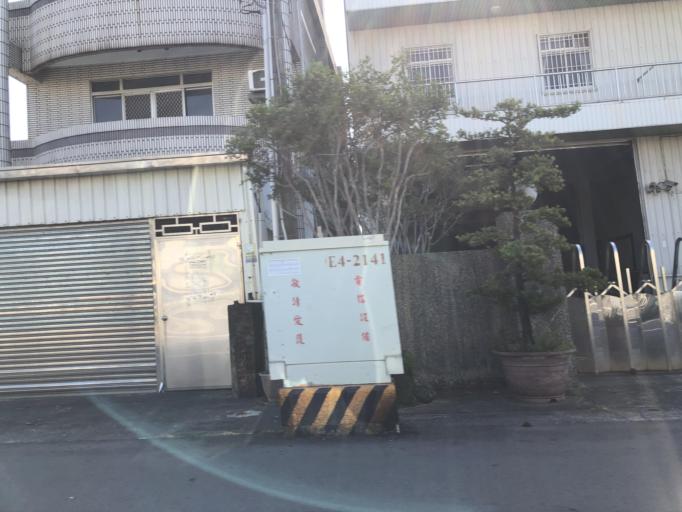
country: TW
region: Taiwan
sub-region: Tainan
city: Tainan
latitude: 23.0022
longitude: 120.2708
